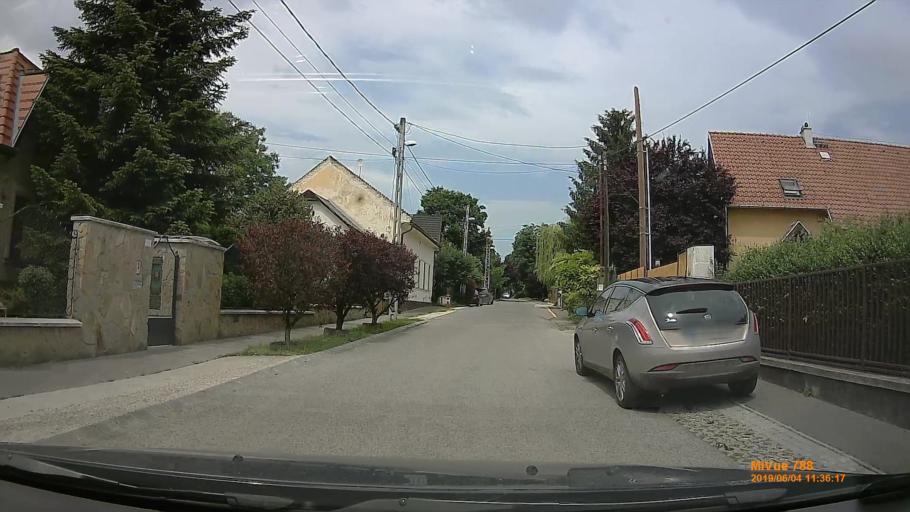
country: HU
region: Budapest
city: Budapest XXII. keruelet
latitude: 47.4396
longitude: 19.0310
